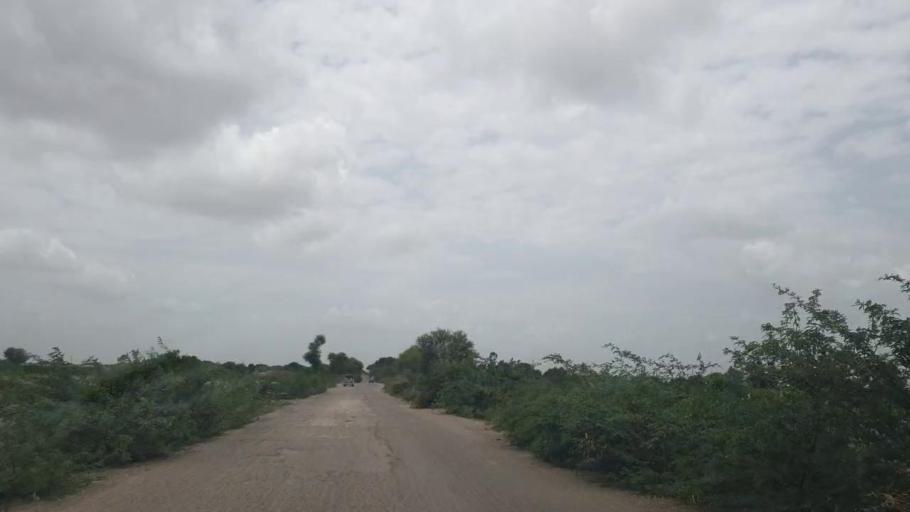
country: PK
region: Sindh
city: Naukot
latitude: 24.9049
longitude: 69.2630
